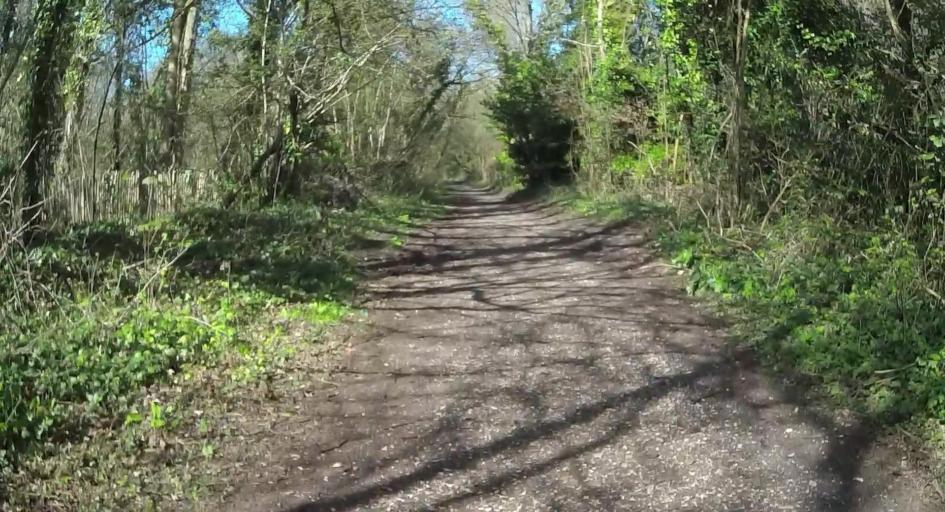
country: GB
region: England
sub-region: Hampshire
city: Abbotts Ann
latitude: 51.0993
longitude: -1.4954
